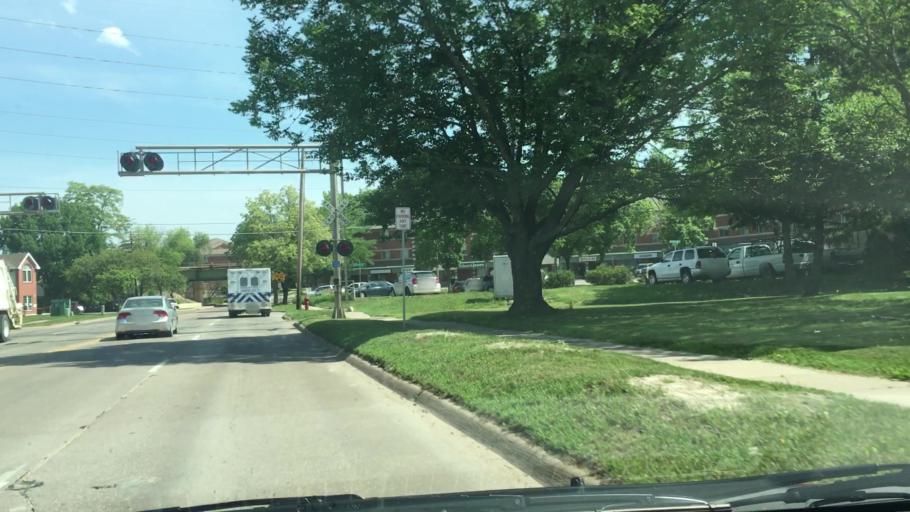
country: US
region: Iowa
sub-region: Johnson County
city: Iowa City
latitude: 41.6518
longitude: -91.5314
